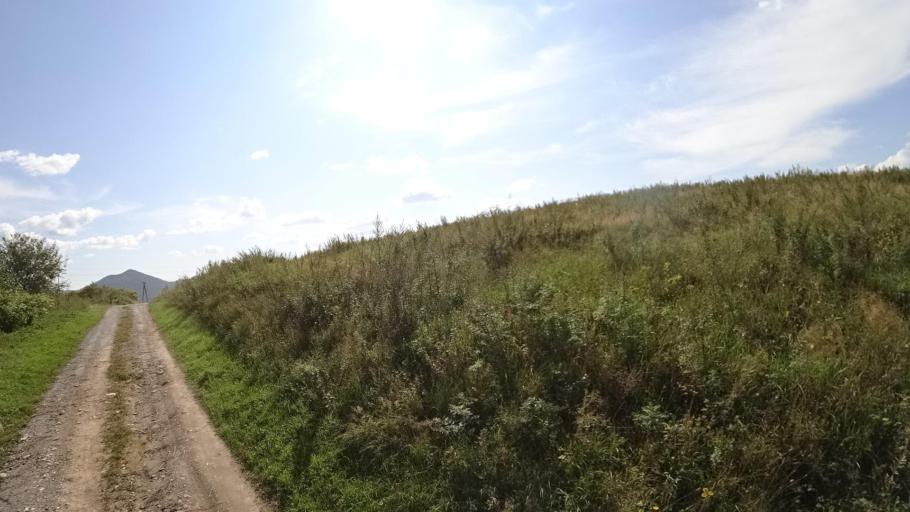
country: RU
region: Jewish Autonomous Oblast
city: Londoko
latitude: 49.0082
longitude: 131.8660
